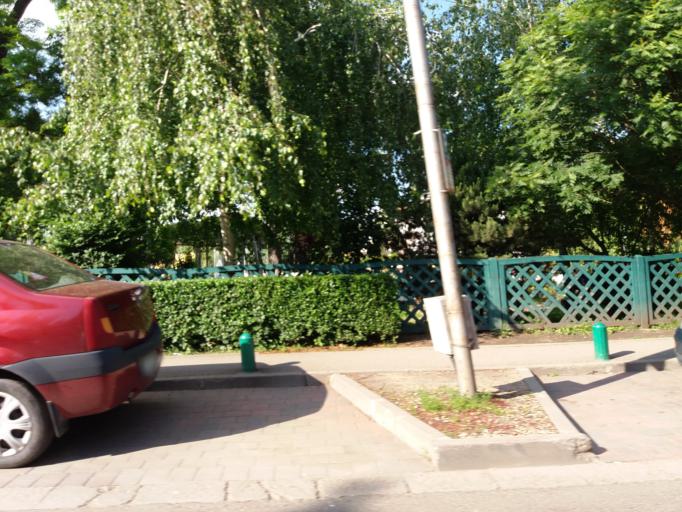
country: RO
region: Arad
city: Arad
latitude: 46.1833
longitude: 21.3225
